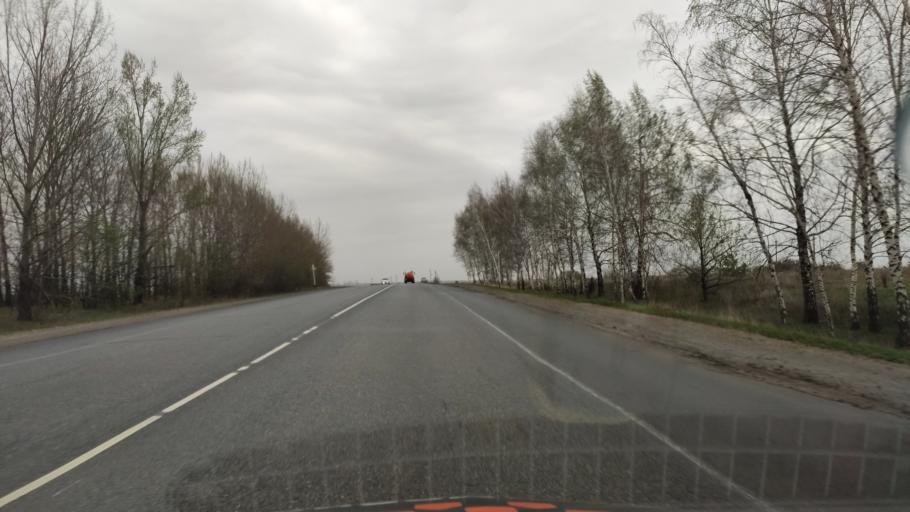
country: RU
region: Kursk
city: Gorshechnoye
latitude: 51.4840
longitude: 37.9630
